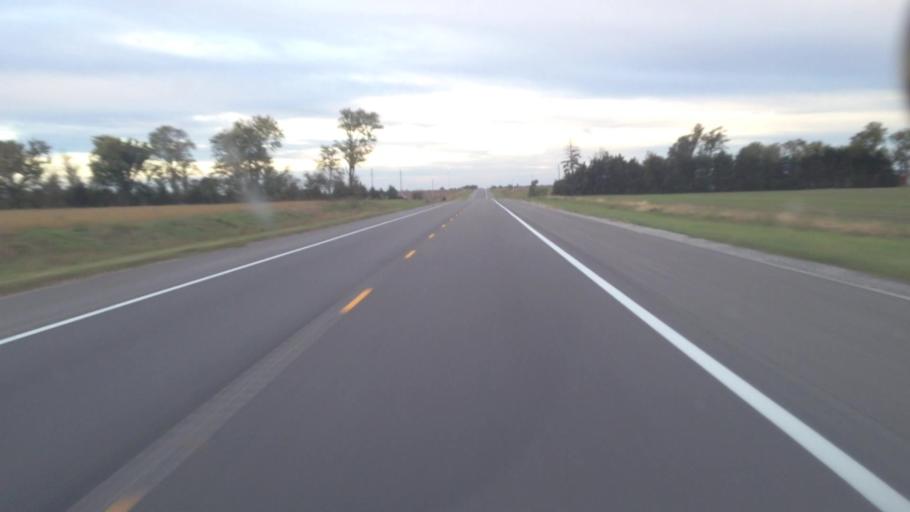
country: US
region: Kansas
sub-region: Franklin County
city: Ottawa
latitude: 38.4540
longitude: -95.2489
